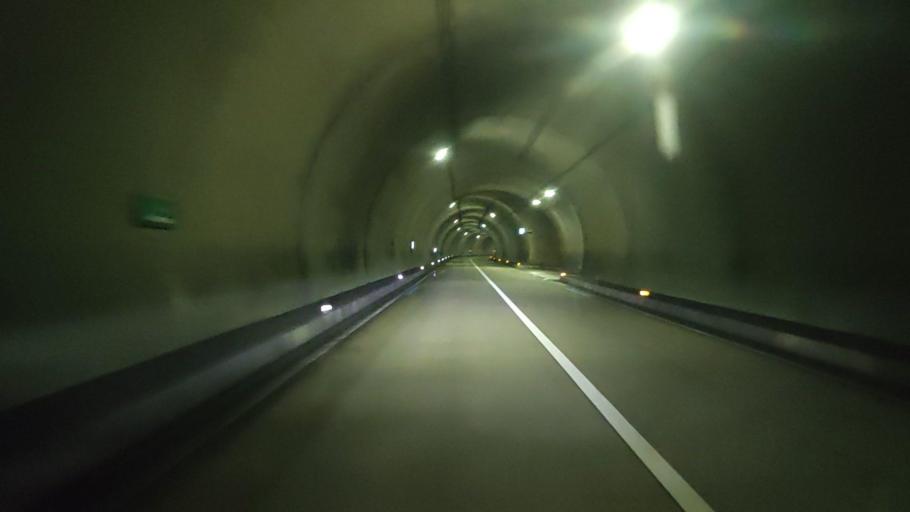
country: JP
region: Wakayama
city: Shingu
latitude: 33.8562
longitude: 135.8526
